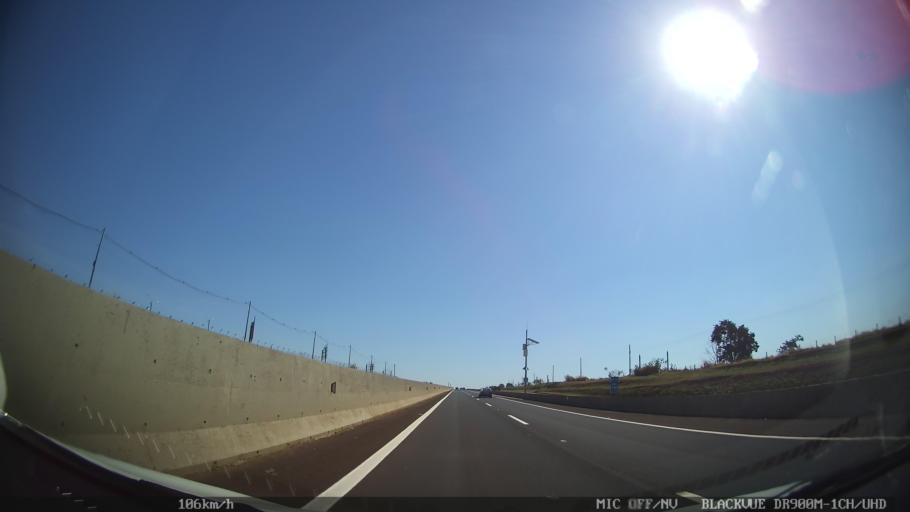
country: BR
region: Sao Paulo
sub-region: Ribeirao Preto
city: Ribeirao Preto
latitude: -21.2039
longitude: -47.8636
